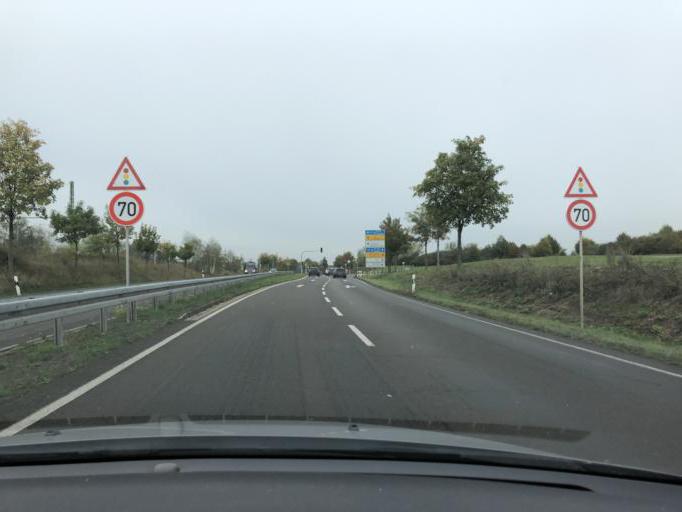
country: DE
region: Saxony
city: Schkeuditz
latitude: 51.3965
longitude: 12.2760
